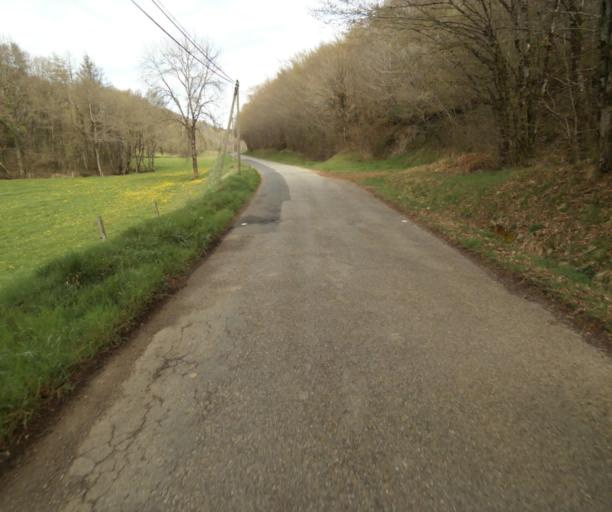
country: FR
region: Limousin
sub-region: Departement de la Correze
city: Laguenne
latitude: 45.2405
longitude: 1.8458
